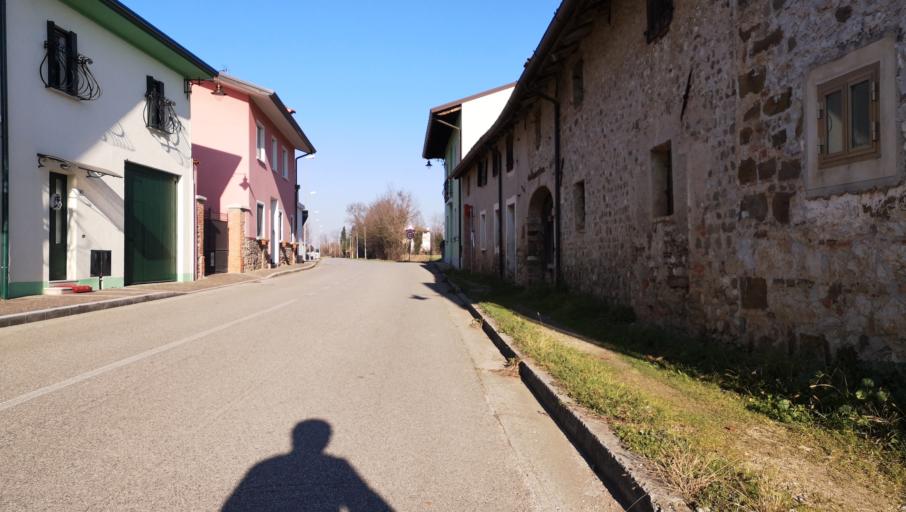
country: IT
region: Friuli Venezia Giulia
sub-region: Provincia di Udine
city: Santa Maria la Longa
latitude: 45.9332
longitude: 13.2822
